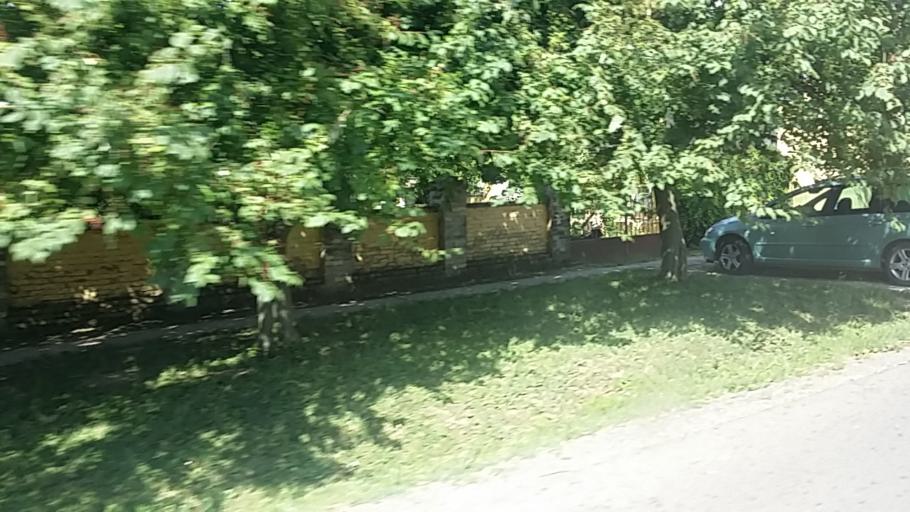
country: HU
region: Baranya
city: Villany
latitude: 45.9013
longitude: 18.3869
